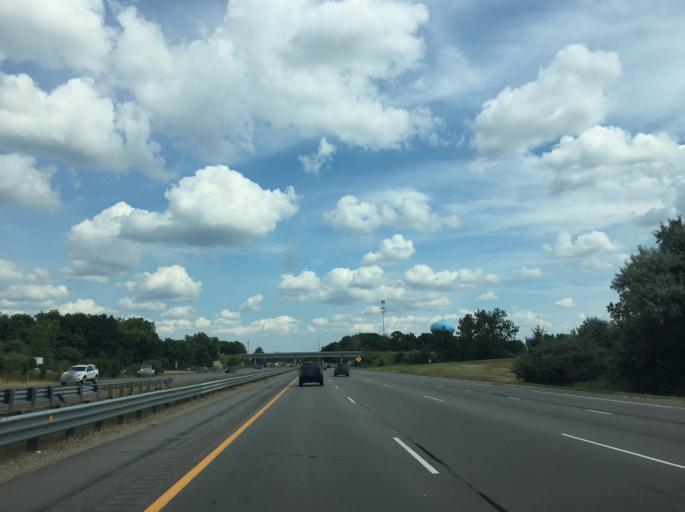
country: US
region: Michigan
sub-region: Oakland County
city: Clarkston
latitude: 42.7358
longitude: -83.3794
